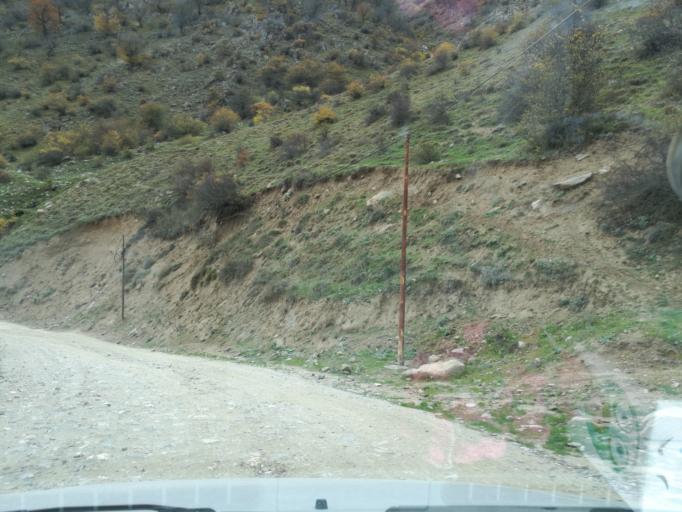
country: IR
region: Mazandaran
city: `Abbasabad
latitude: 36.4365
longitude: 51.0567
